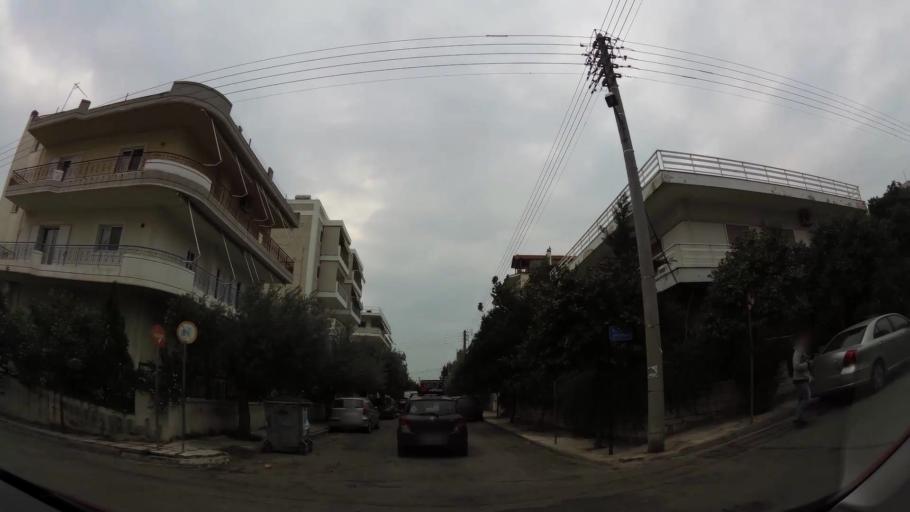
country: GR
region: Attica
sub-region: Nomarchia Athinas
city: Ilion
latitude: 38.0298
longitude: 23.7116
